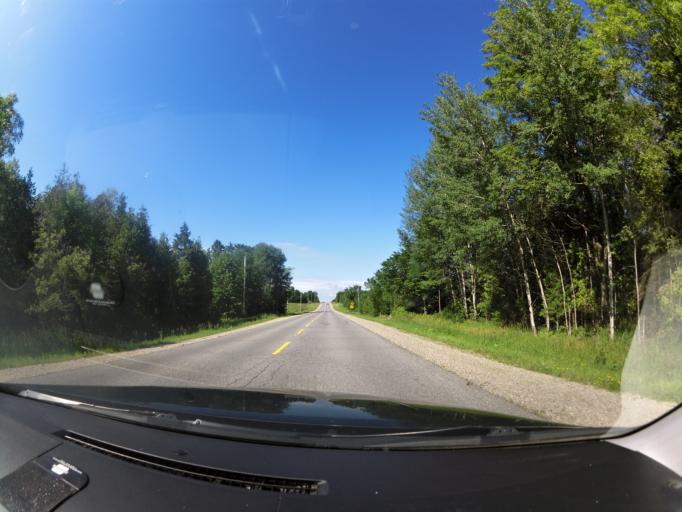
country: CA
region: Ontario
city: Carleton Place
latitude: 45.1279
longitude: -76.3359
